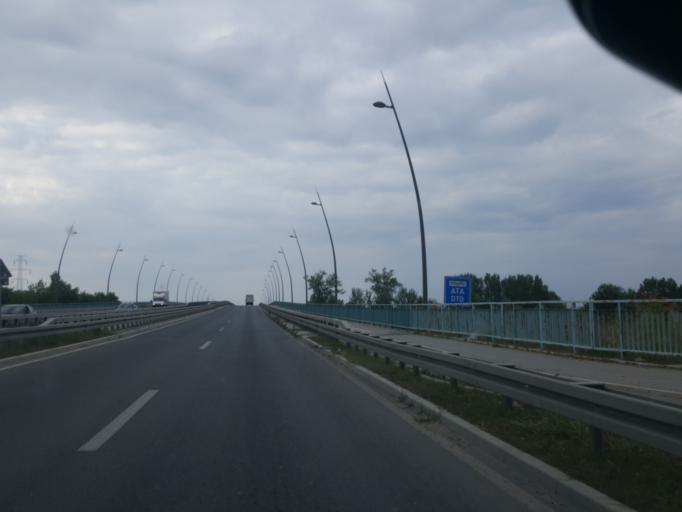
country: RS
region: Autonomna Pokrajina Vojvodina
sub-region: Juznobacki Okrug
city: Novi Sad
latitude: 45.2826
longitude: 19.8036
